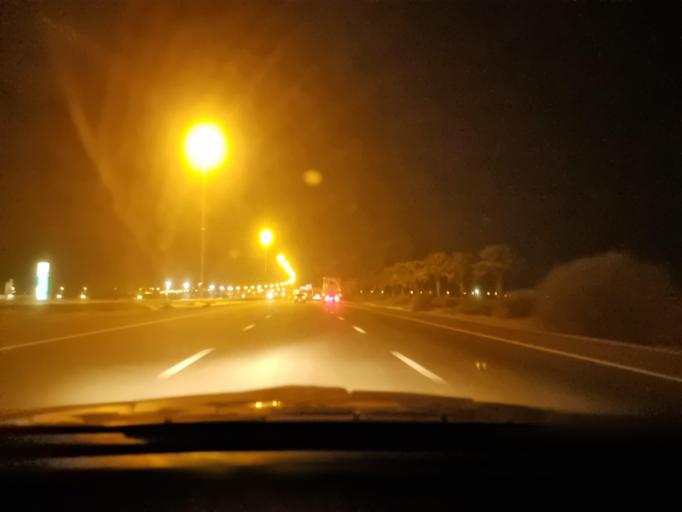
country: AE
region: Dubai
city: Dubai
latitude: 24.8705
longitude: 55.0269
